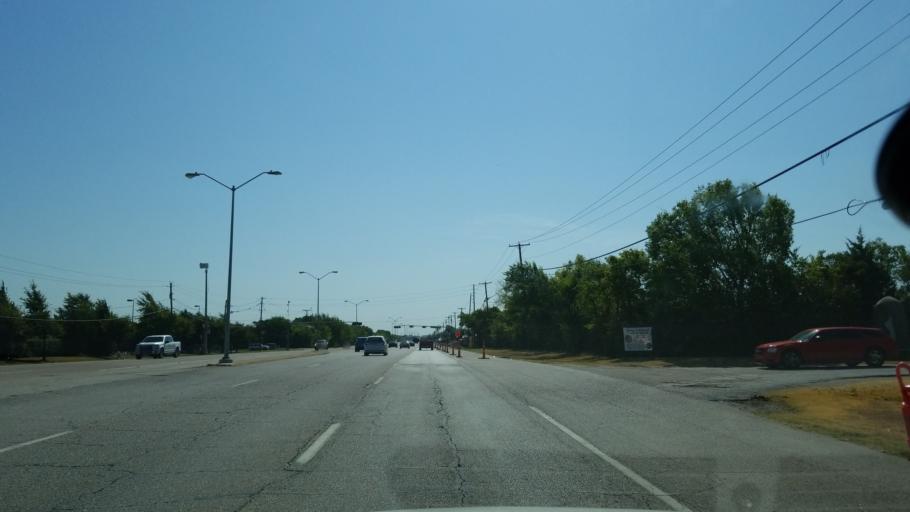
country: US
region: Texas
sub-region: Dallas County
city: Cockrell Hill
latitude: 32.7496
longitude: -96.8933
